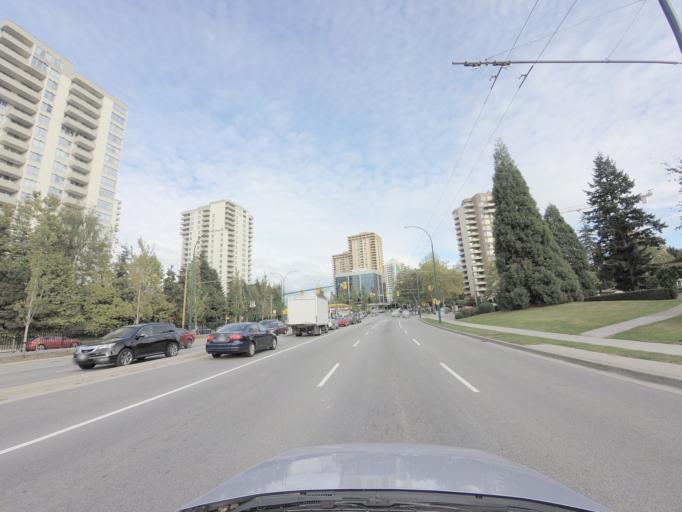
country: CA
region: British Columbia
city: Burnaby
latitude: 49.2327
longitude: -123.0137
